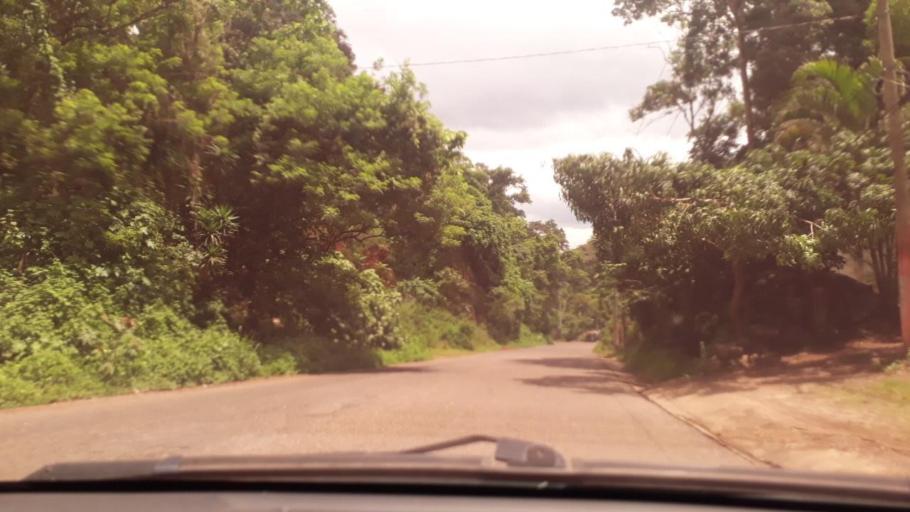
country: GT
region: Santa Rosa
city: Oratorio
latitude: 14.2345
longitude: -90.1887
